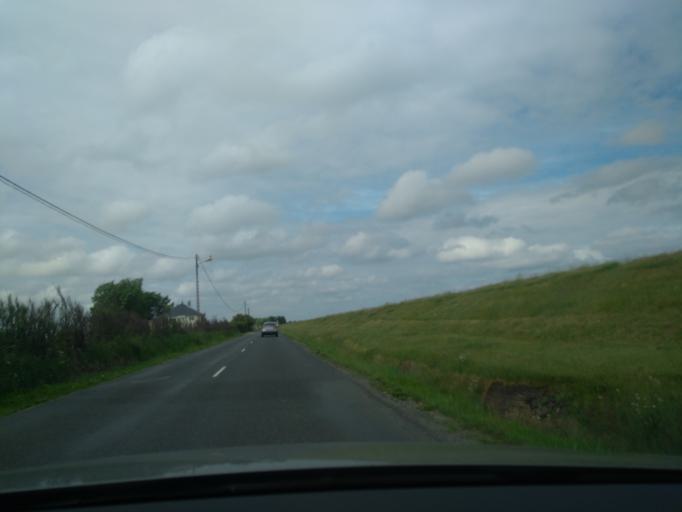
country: FR
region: Lower Normandy
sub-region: Departement de la Manche
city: Saint-Vaast-la-Hougue
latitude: 49.5949
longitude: -1.2656
